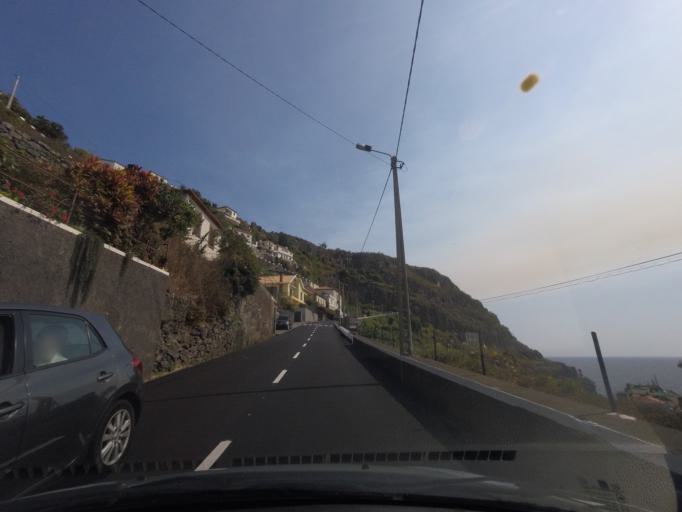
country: PT
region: Madeira
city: Ribeira Brava
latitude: 32.6720
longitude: -17.0627
